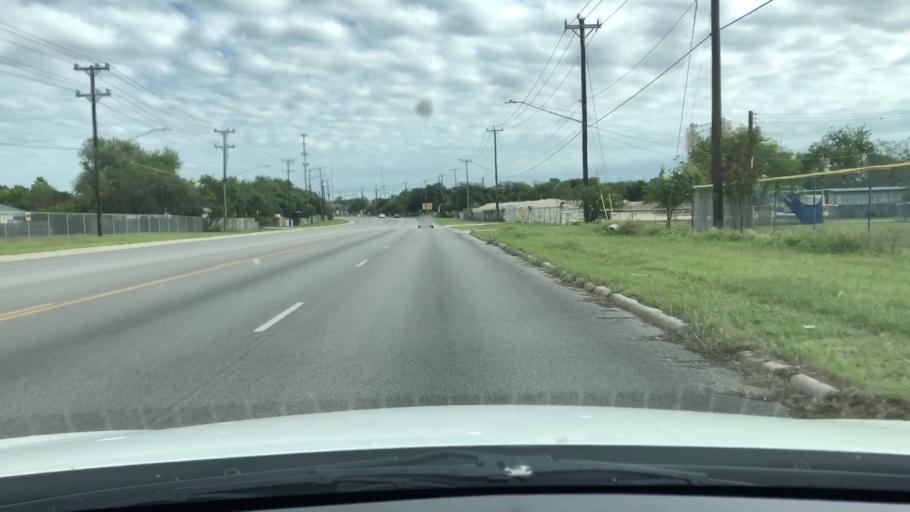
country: US
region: Texas
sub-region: Bexar County
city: Leon Valley
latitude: 29.4782
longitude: -98.6543
